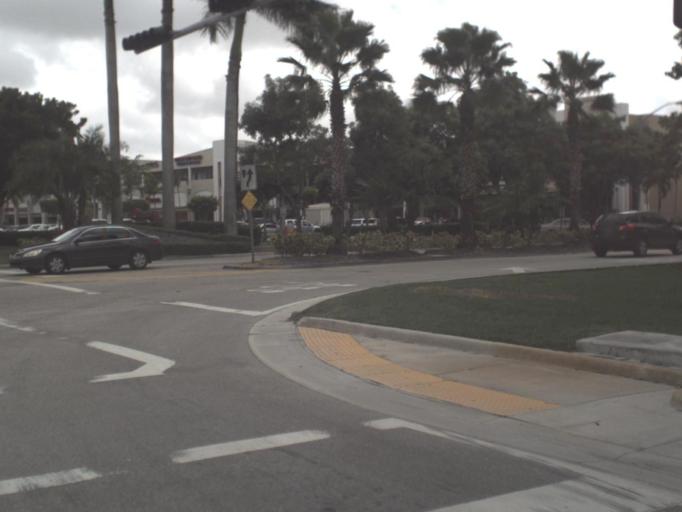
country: US
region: Florida
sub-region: Miami-Dade County
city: Doral
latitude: 25.8116
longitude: -80.3842
